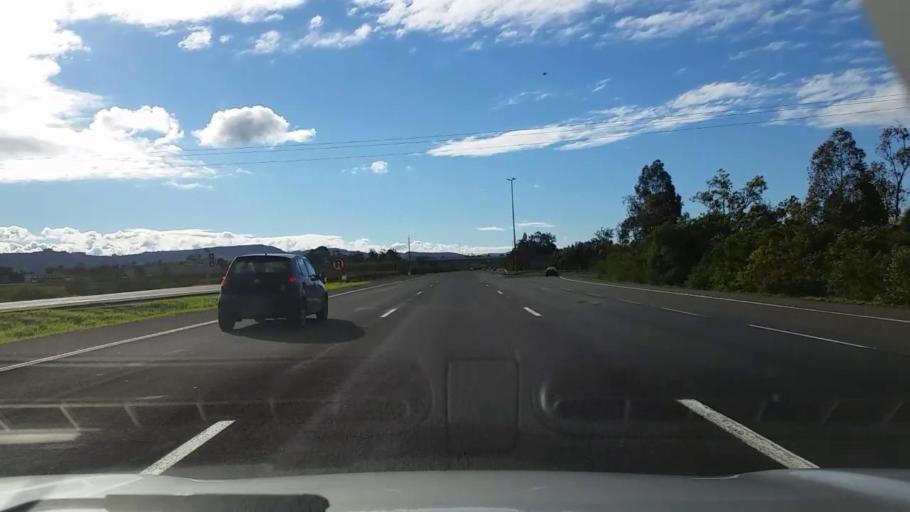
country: BR
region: Rio Grande do Sul
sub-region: Rolante
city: Rolante
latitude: -29.8807
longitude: -50.5154
